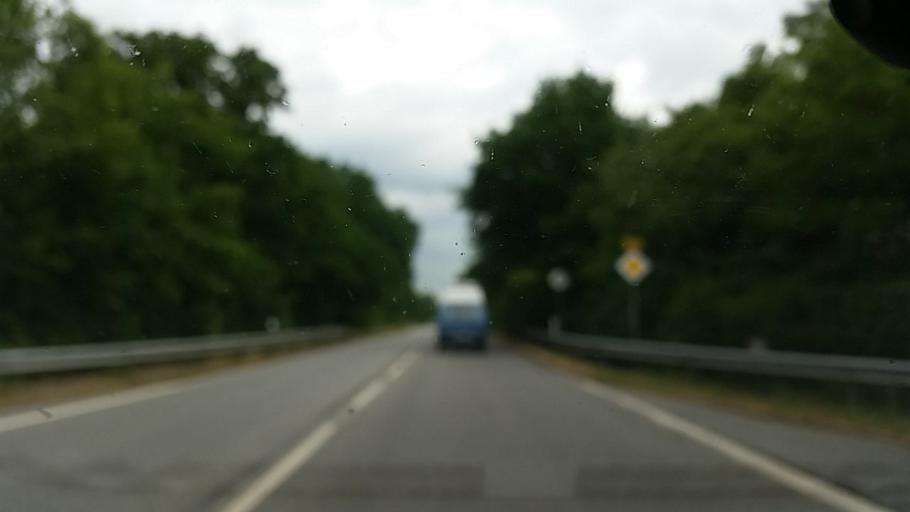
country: DE
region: Schleswig-Holstein
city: Elmenhorst
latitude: 53.7763
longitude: 10.2734
